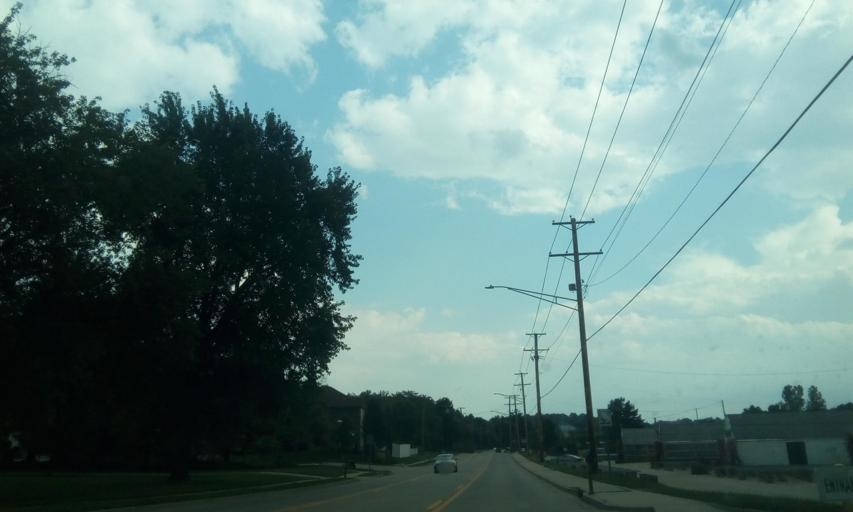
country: US
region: Missouri
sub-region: Saint Louis County
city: Town and Country
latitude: 38.5881
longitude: -90.4693
